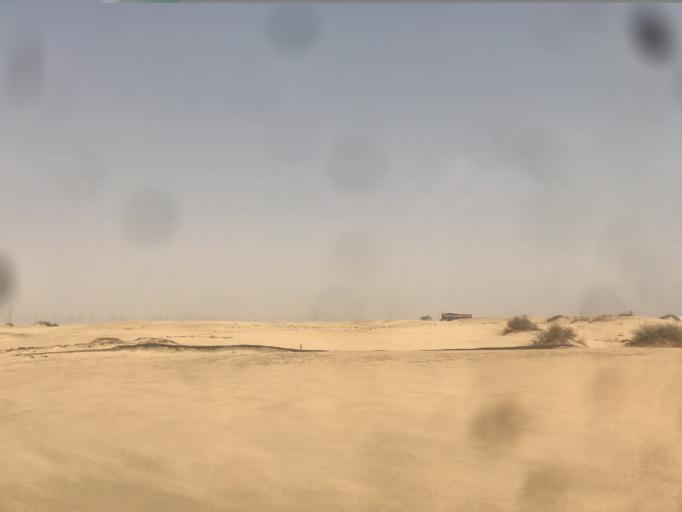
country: SA
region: Eastern Province
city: Abqaiq
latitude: 25.9084
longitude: 49.9256
